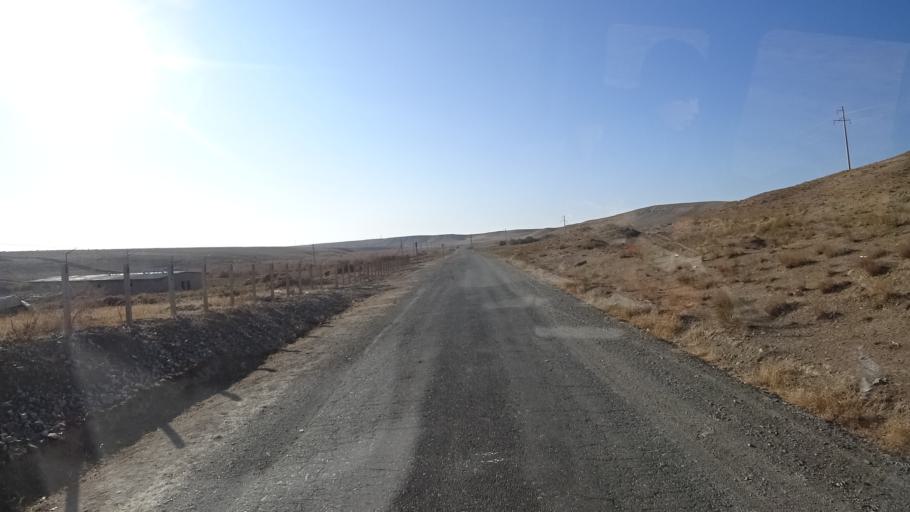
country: UZ
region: Navoiy
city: Beshrabot
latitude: 40.2577
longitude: 65.4550
